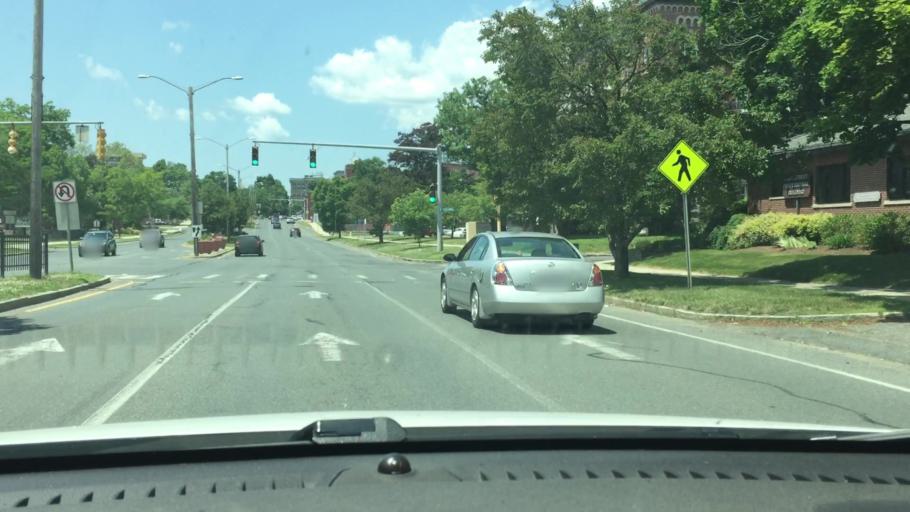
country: US
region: Massachusetts
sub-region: Berkshire County
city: Pittsfield
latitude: 42.4476
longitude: -73.2480
